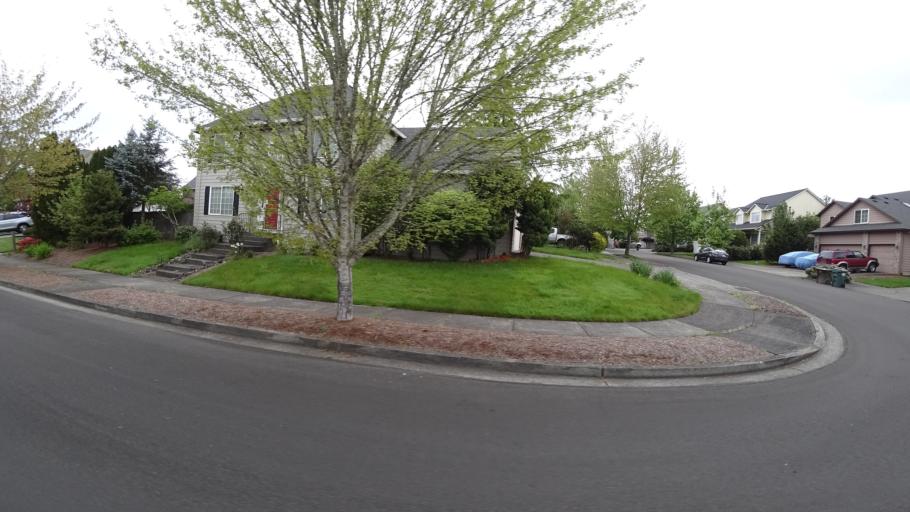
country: US
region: Oregon
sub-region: Washington County
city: Hillsboro
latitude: 45.5472
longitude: -122.9700
